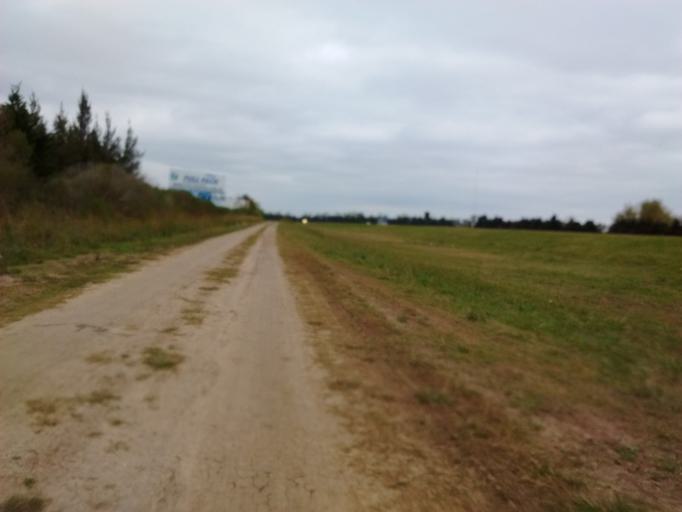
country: AR
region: Santa Fe
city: Funes
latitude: -32.9355
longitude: -60.8308
